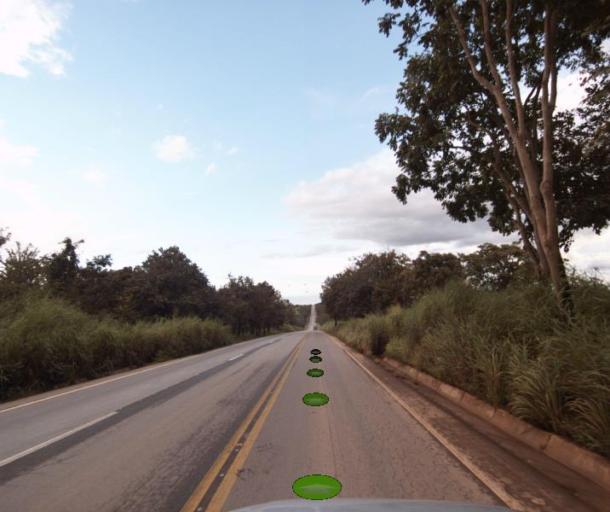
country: BR
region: Goias
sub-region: Porangatu
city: Porangatu
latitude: -13.4683
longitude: -49.1359
